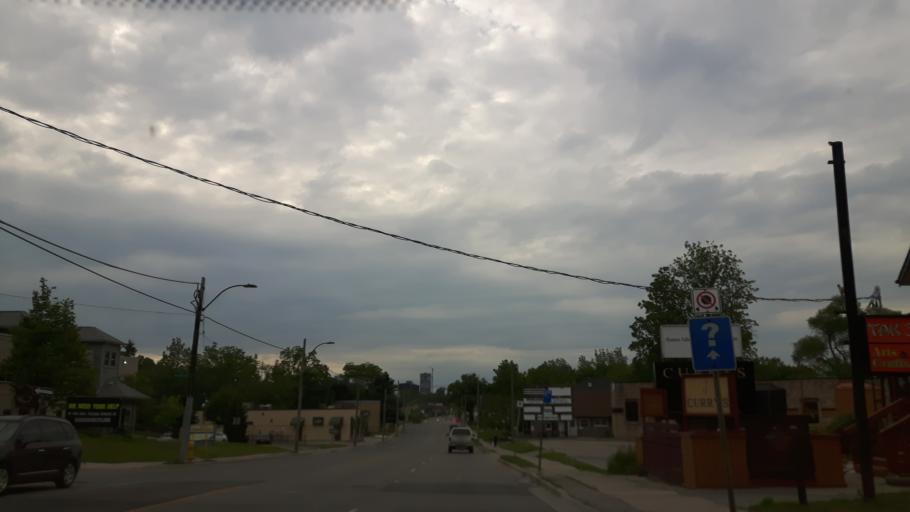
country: CA
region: Ontario
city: London
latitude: 42.9704
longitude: -81.2365
